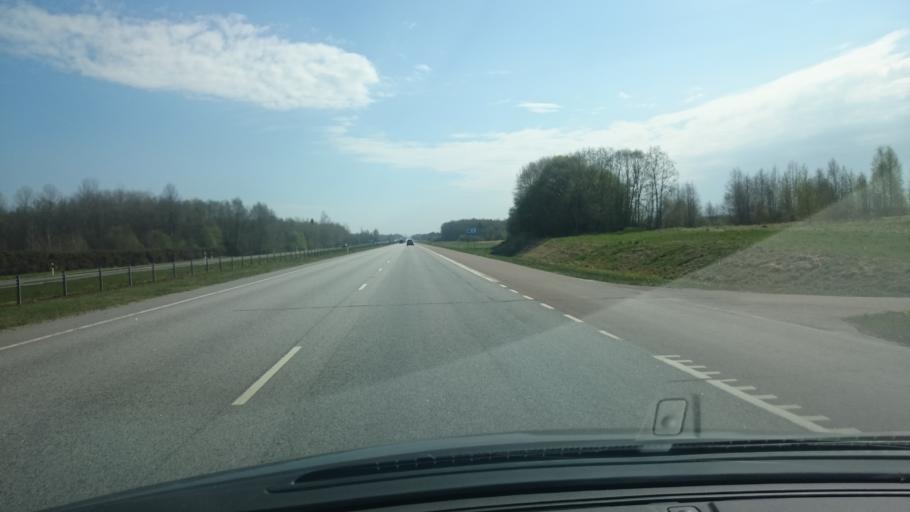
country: EE
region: Harju
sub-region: Kuusalu vald
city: Kuusalu
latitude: 59.4429
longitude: 25.3358
